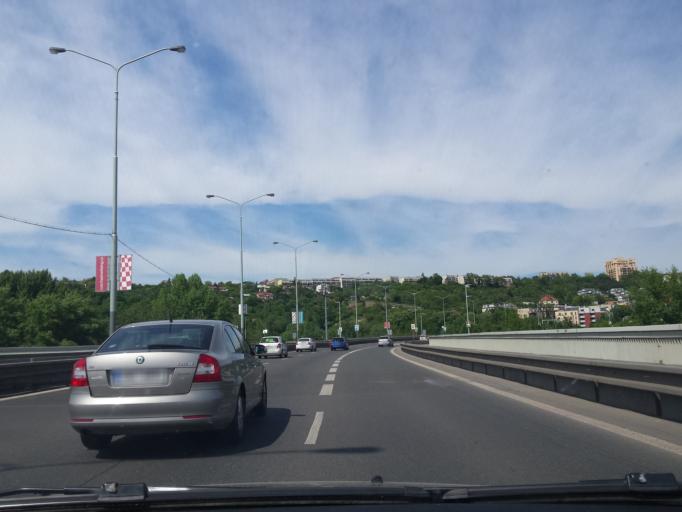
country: CZ
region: Praha
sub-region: Praha 8
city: Karlin
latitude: 50.1134
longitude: 14.4455
